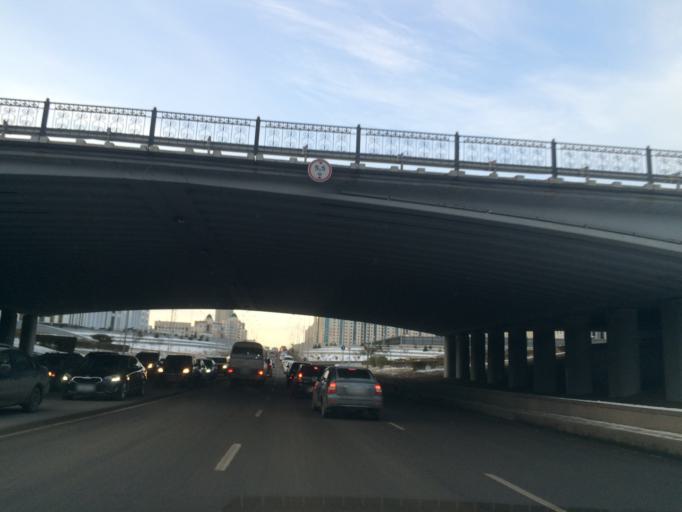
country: KZ
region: Astana Qalasy
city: Astana
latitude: 51.1225
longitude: 71.4365
